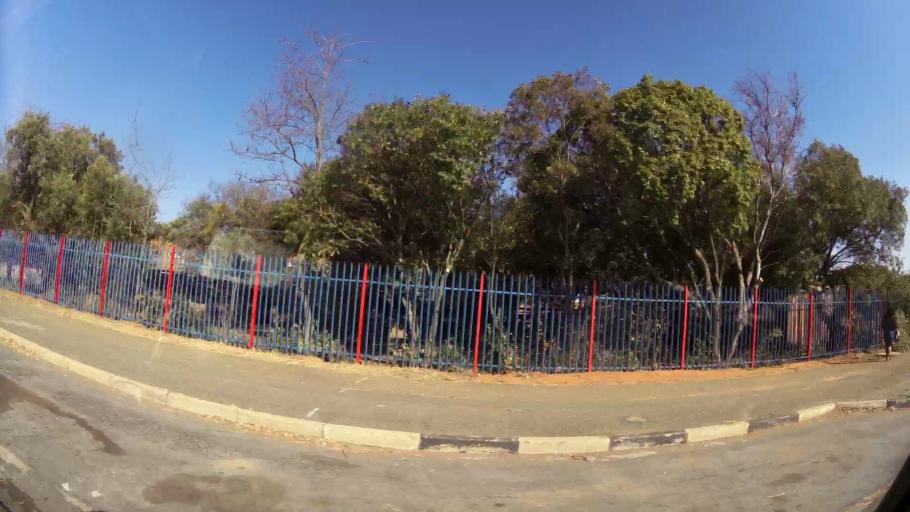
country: ZA
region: Gauteng
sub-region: City of Johannesburg Metropolitan Municipality
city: Johannesburg
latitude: -26.2570
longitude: 28.0001
